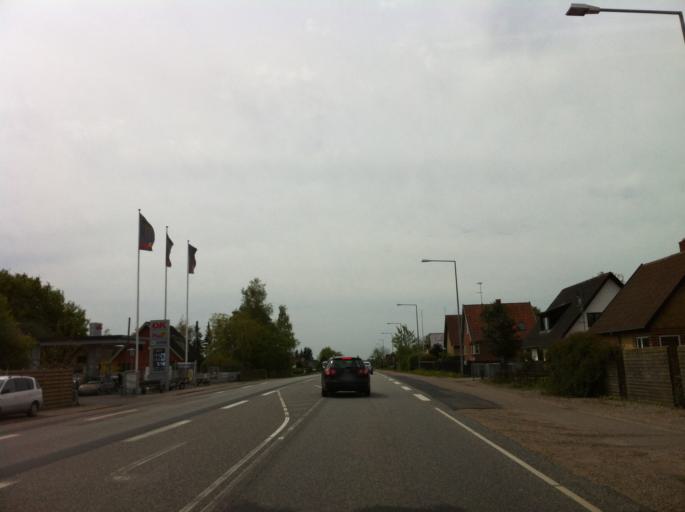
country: DK
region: Zealand
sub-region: Ringsted Kommune
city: Ringsted
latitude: 55.4860
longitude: 11.8519
